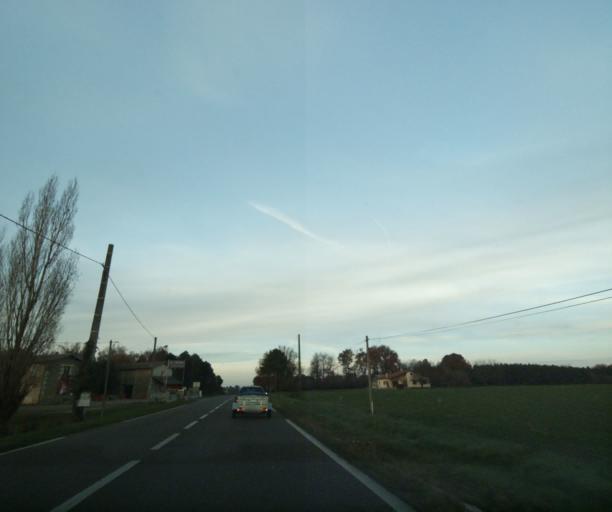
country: FR
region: Aquitaine
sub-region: Departement de la Gironde
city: Langon
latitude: 44.5017
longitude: -0.2382
